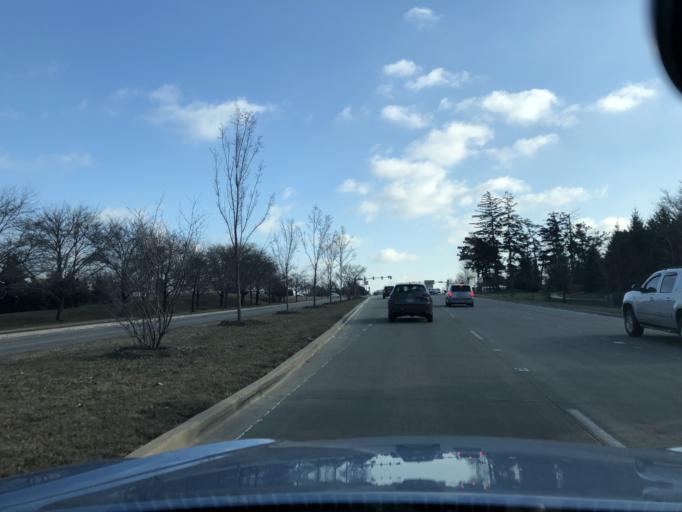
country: US
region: Illinois
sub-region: Cook County
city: Northfield
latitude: 42.1054
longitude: -87.8021
